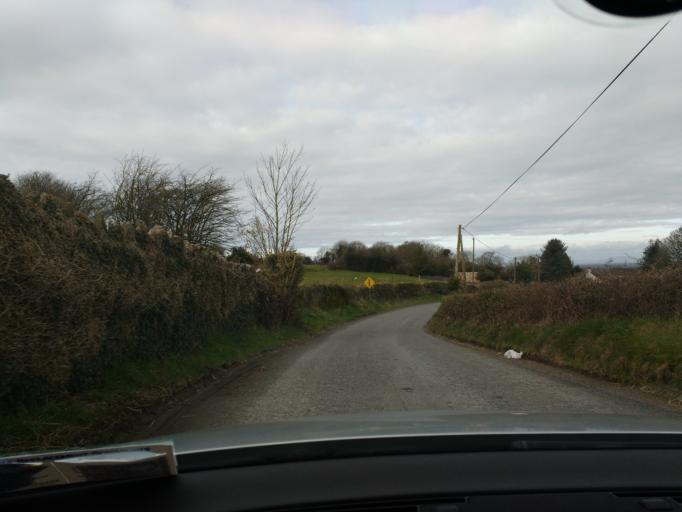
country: IE
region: Leinster
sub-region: Kilkenny
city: Callan
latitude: 52.6573
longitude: -7.5486
